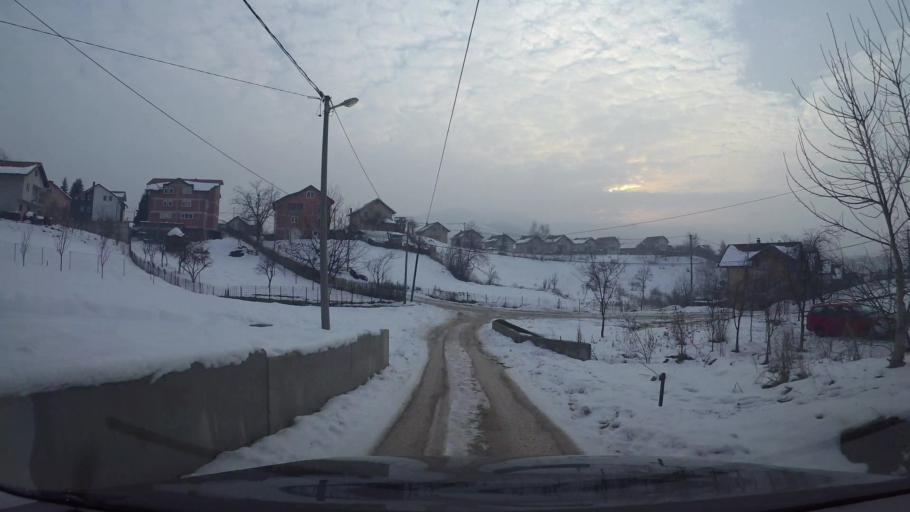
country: BA
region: Federation of Bosnia and Herzegovina
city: Hotonj
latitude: 43.8966
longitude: 18.3783
